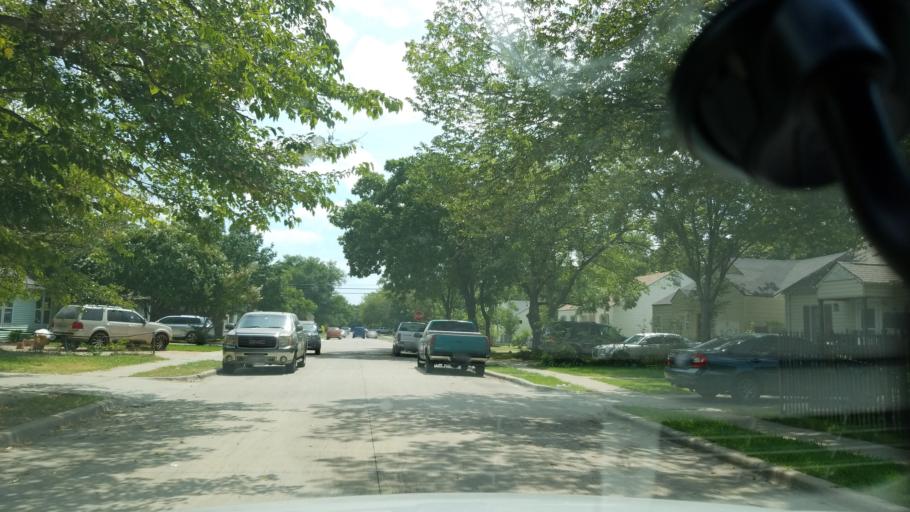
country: US
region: Texas
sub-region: Dallas County
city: Grand Prairie
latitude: 32.7538
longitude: -96.9849
